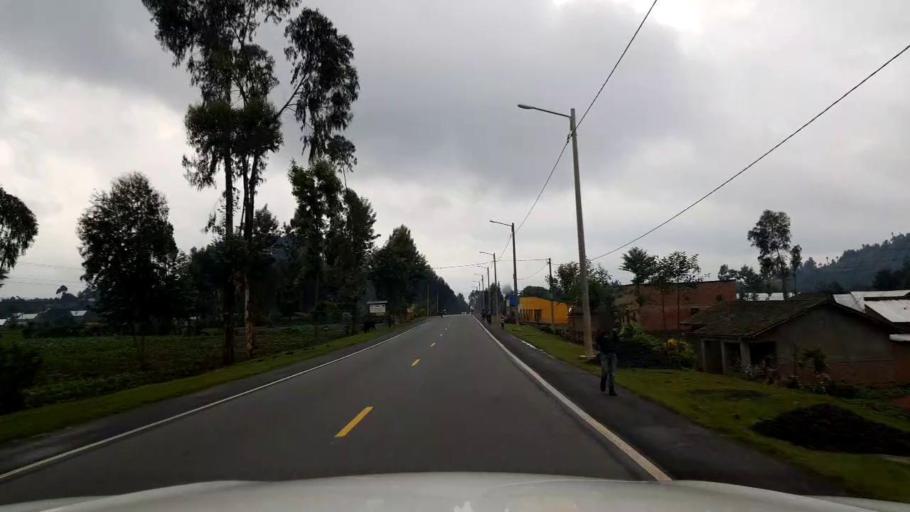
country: RW
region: Northern Province
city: Musanze
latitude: -1.5436
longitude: 29.5592
